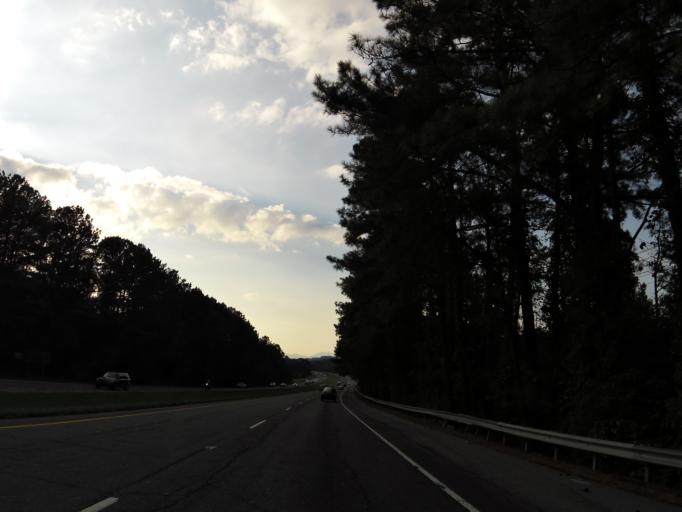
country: US
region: Tennessee
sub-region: Knox County
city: Farragut
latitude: 35.9442
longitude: -84.1543
